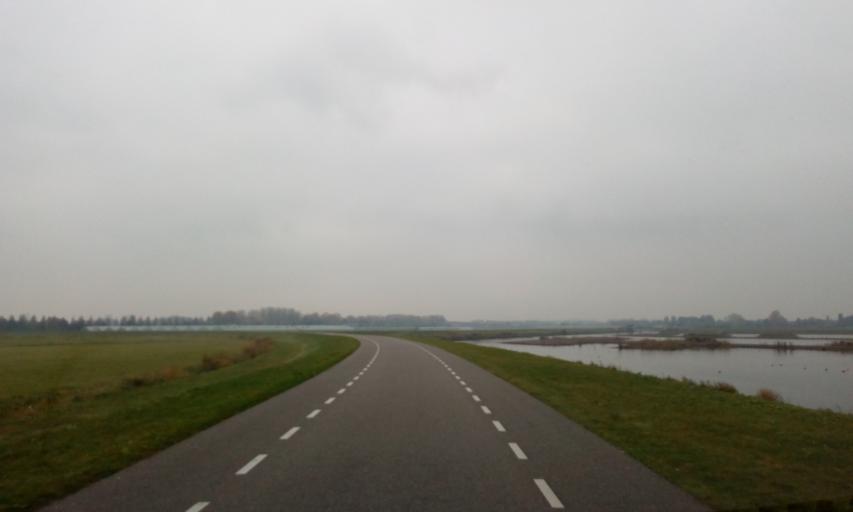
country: NL
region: South Holland
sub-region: Gemeente Lansingerland
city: Bleiswijk
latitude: 51.9914
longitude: 4.5658
